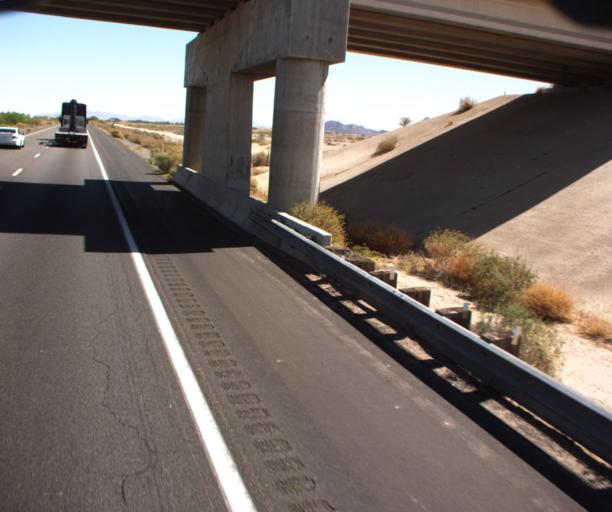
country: US
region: Arizona
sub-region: Yuma County
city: Wellton
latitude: 32.6742
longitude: -114.0738
